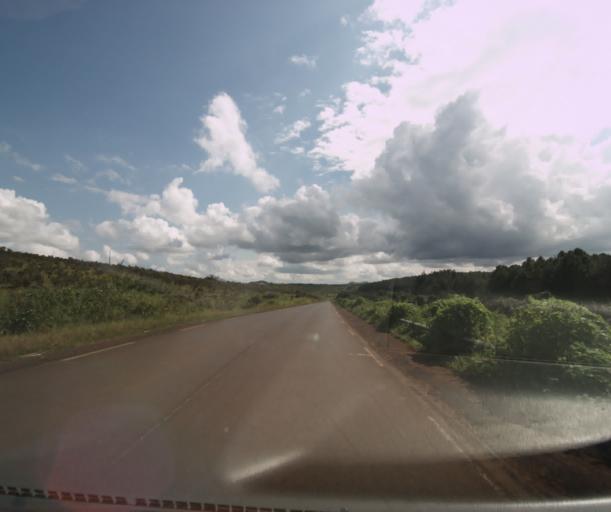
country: CM
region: West
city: Foumban
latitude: 5.7030
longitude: 10.8305
